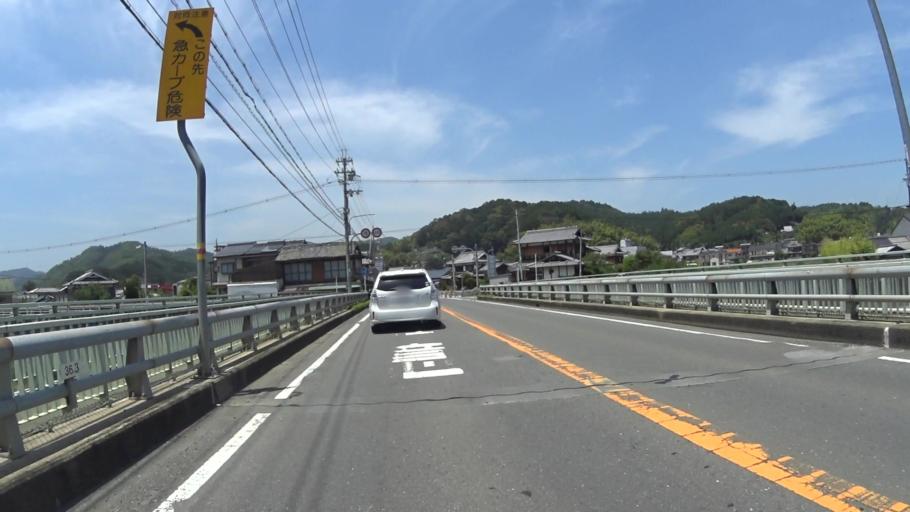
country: JP
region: Kyoto
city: Kameoka
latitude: 35.1107
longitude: 135.4703
